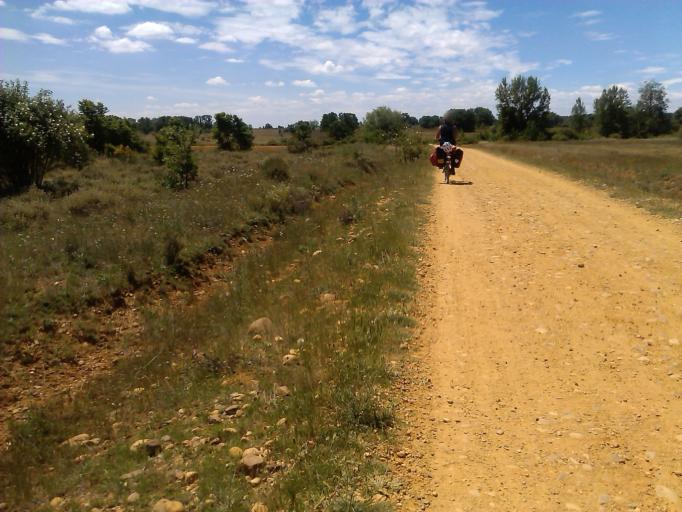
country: ES
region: Castille and Leon
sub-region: Provincia de Leon
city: Valverde de la Virgen
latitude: 42.5397
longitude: -5.6638
